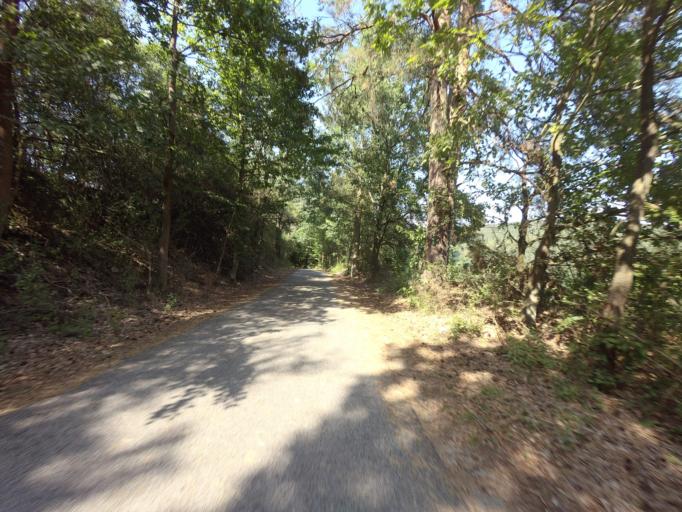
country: CZ
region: Jihocesky
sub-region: Okres Ceske Budejovice
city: Hluboka nad Vltavou
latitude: 49.1150
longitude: 14.4587
